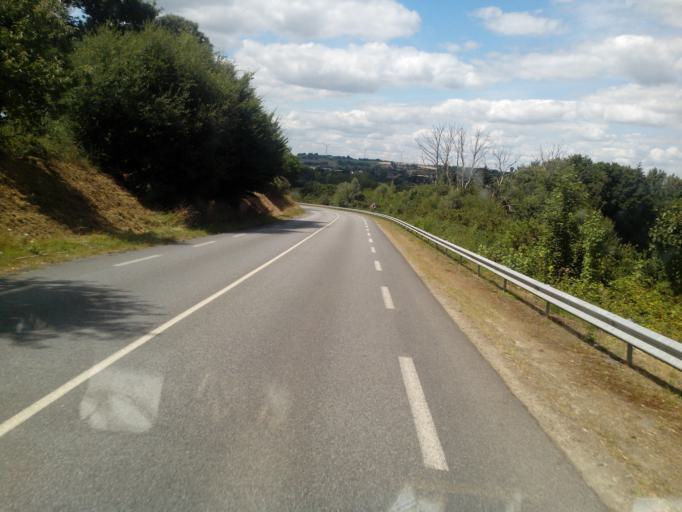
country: FR
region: Brittany
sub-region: Departement du Morbihan
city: Guegon
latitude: 47.9485
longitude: -2.5579
